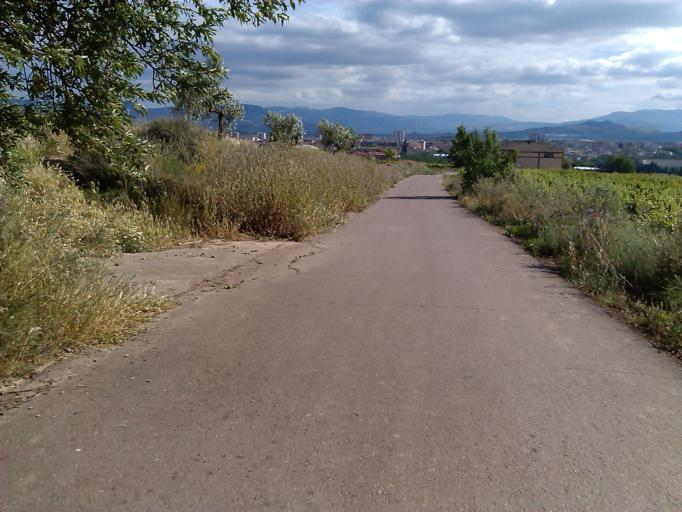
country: ES
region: La Rioja
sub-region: Provincia de La Rioja
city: Logrono
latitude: 42.4810
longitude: -2.4351
